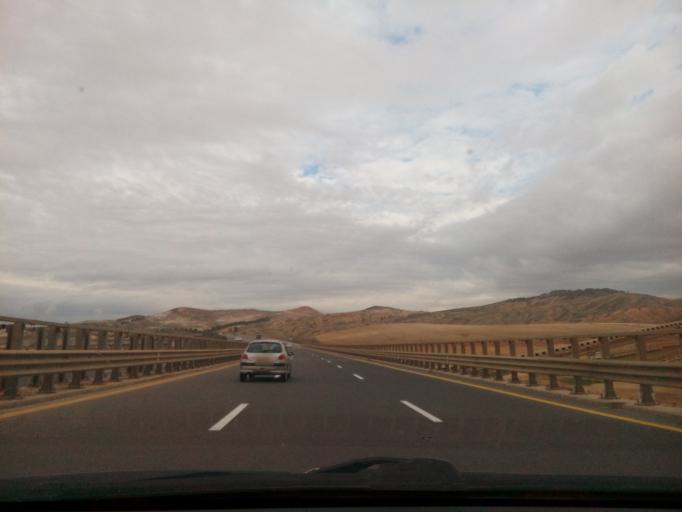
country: DZ
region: Sidi Bel Abbes
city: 'Ain el Berd
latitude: 35.4548
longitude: -0.3901
